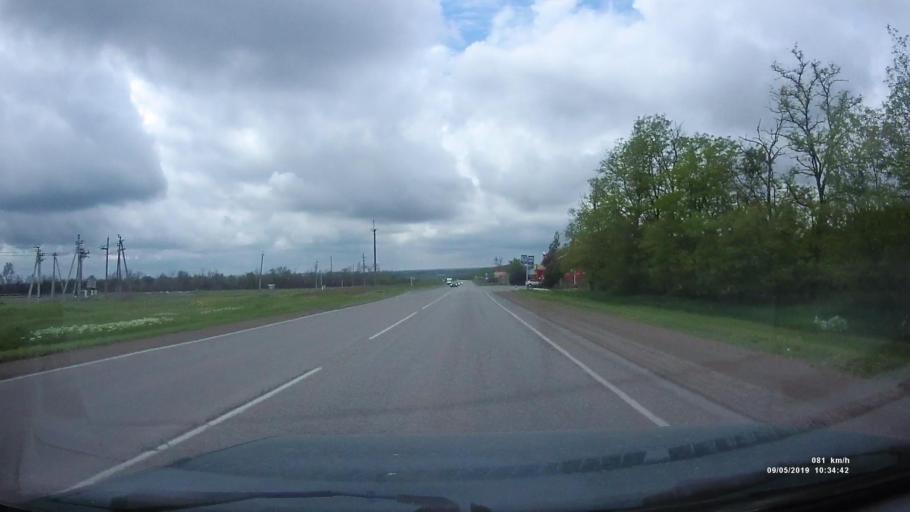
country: RU
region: Rostov
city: Peshkovo
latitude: 47.0510
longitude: 39.4175
